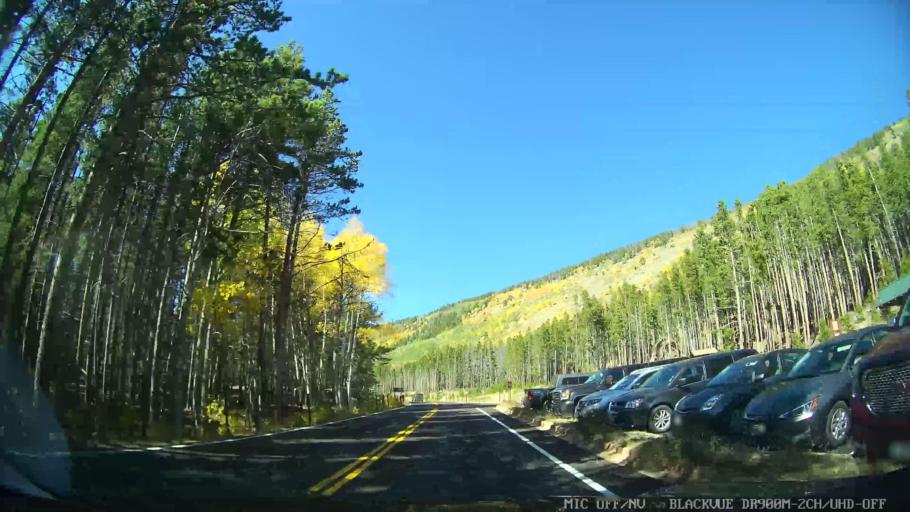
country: US
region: Colorado
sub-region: Larimer County
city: Estes Park
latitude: 40.3203
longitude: -105.6232
